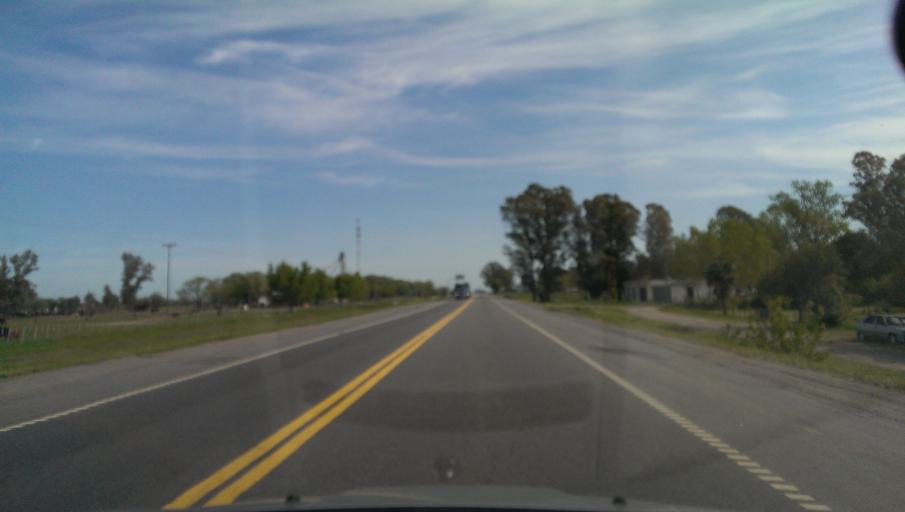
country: AR
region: Buenos Aires
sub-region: Partido de Azul
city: Azul
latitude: -36.3894
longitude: -59.4947
